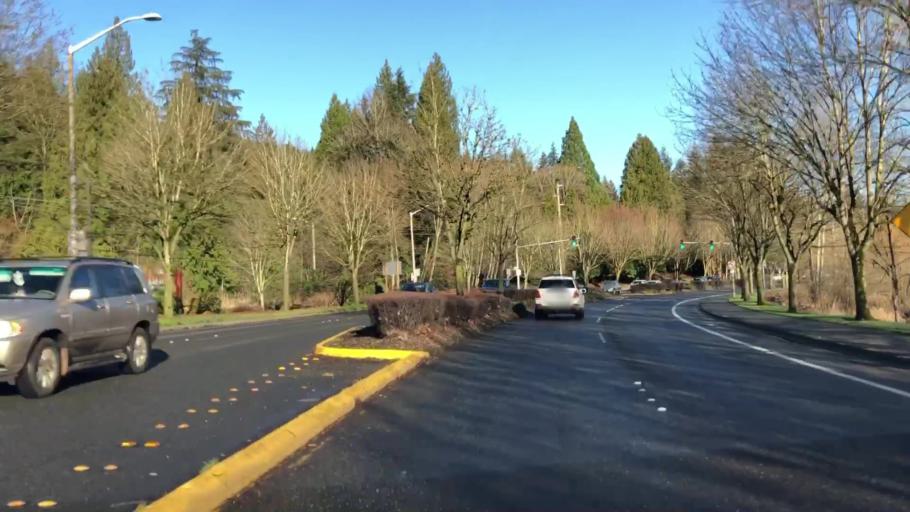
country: US
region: Washington
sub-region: King County
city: Redmond
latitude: 47.6766
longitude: -122.1060
